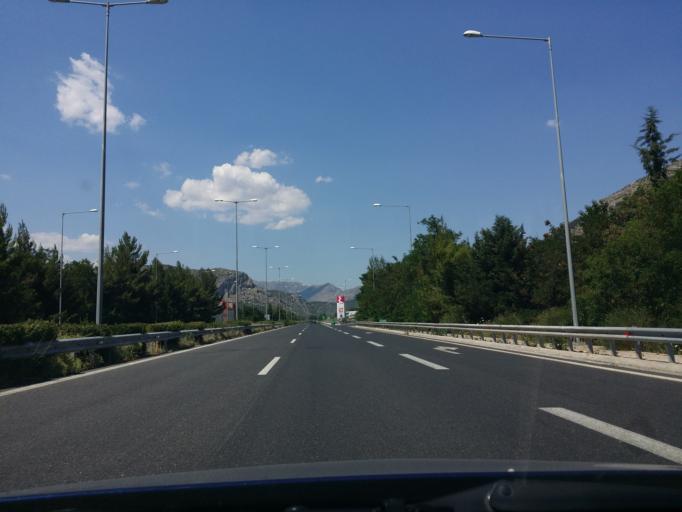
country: GR
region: Peloponnese
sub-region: Nomos Arkadias
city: Tripoli
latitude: 37.5775
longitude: 22.4306
